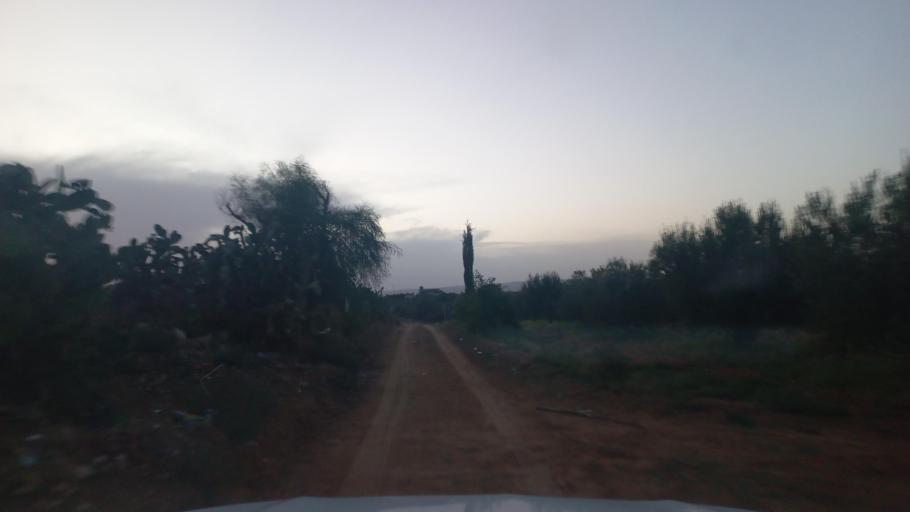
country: TN
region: Al Qasrayn
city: Kasserine
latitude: 35.2312
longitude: 9.0343
